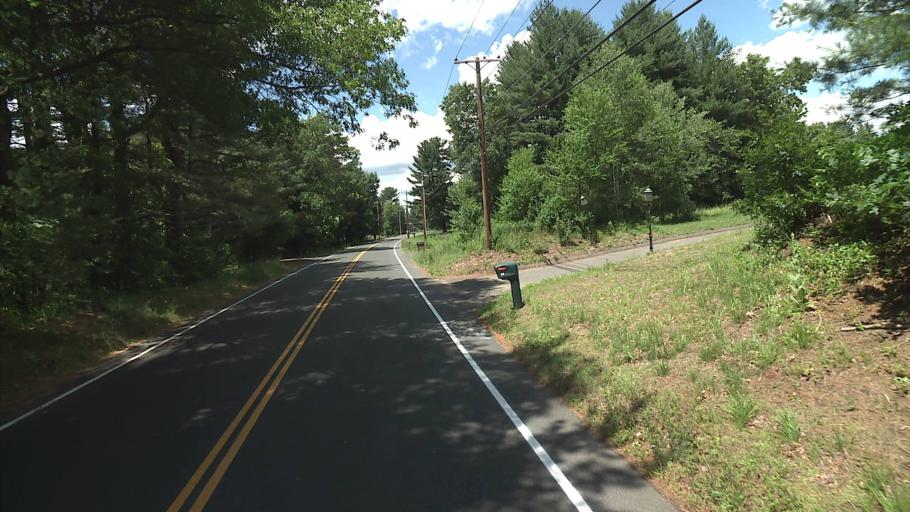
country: US
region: Connecticut
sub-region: Tolland County
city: Somers
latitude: 41.9921
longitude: -72.4850
